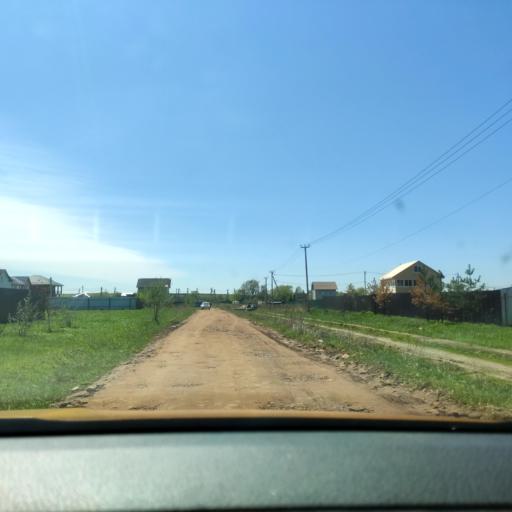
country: RU
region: Moskovskaya
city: Beloozerskiy
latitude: 55.3698
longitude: 38.4027
